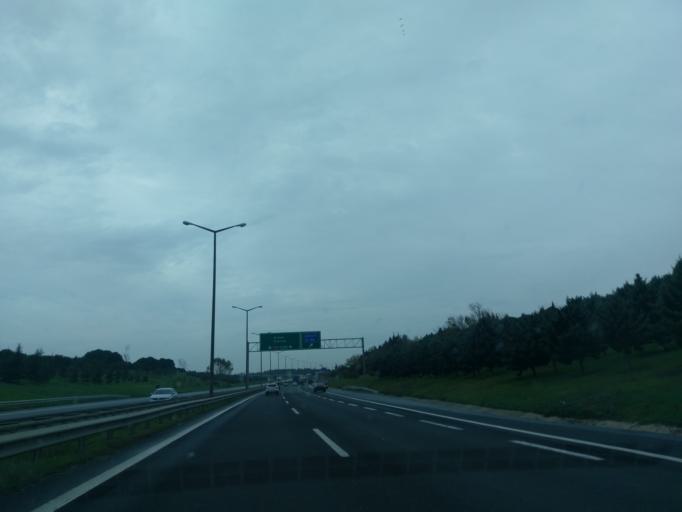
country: TR
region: Istanbul
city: Silivri
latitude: 41.1076
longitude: 28.2734
